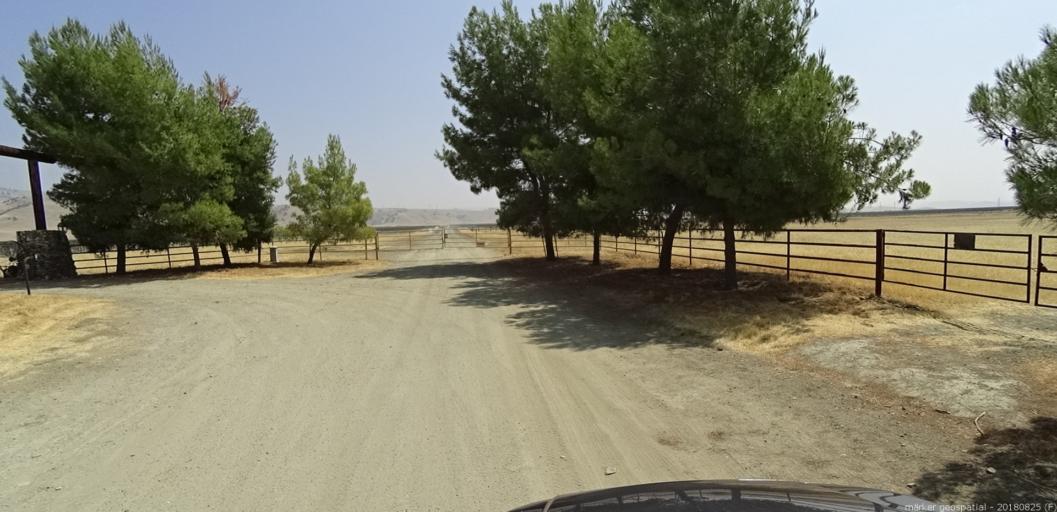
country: US
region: California
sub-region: San Luis Obispo County
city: Shandon
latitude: 35.8774
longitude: -120.3512
